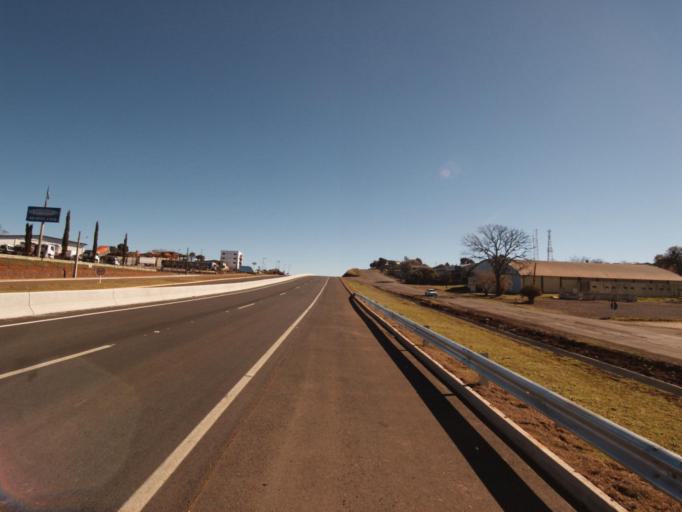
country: BR
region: Santa Catarina
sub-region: Xanxere
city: Xanxere
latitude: -26.8856
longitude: -52.4164
